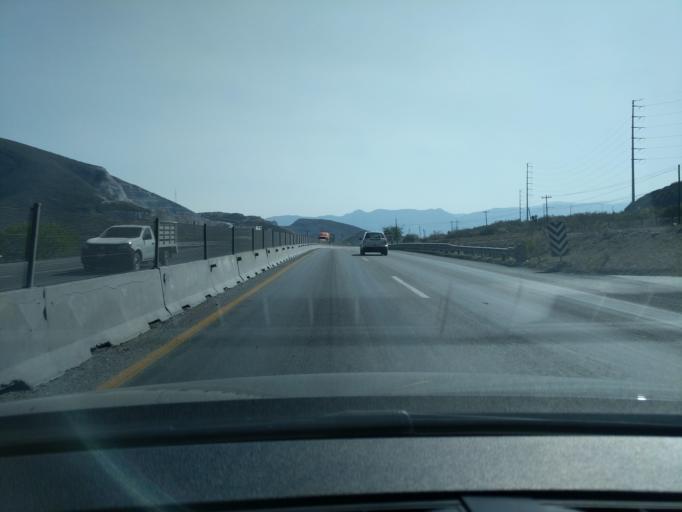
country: MX
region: Nuevo Leon
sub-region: Garcia
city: Los Parques
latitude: 25.7587
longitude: -100.4974
